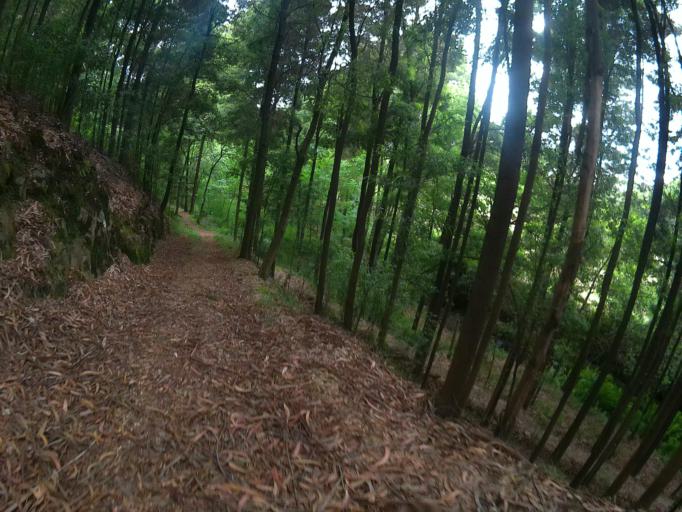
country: PT
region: Aveiro
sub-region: Albergaria-A-Velha
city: Branca
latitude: 40.7663
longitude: -8.4444
